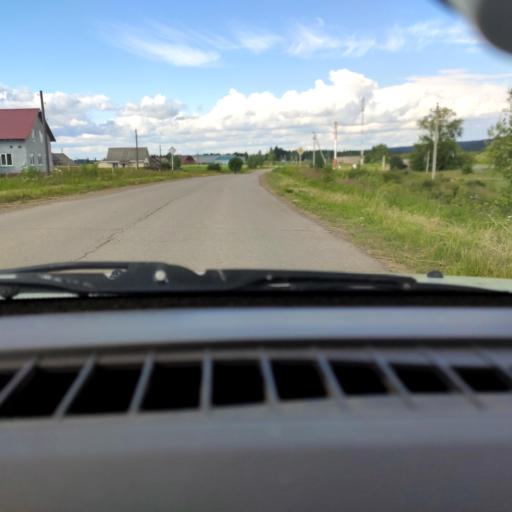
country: RU
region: Perm
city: Uinskoye
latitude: 57.1811
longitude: 56.5603
